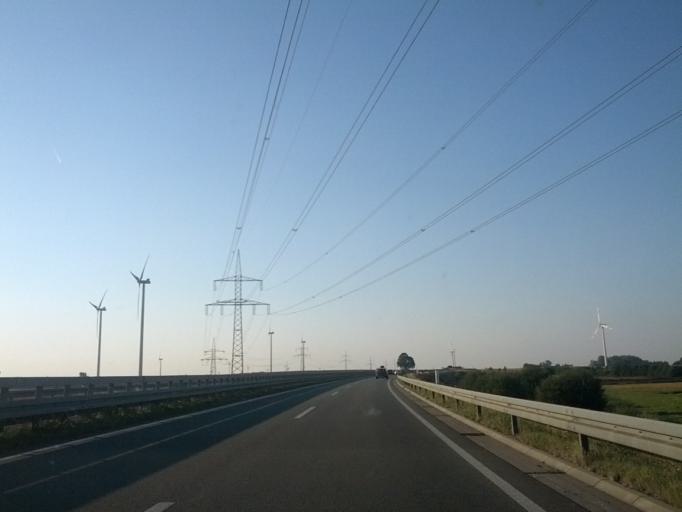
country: DE
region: Mecklenburg-Vorpommern
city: Brandshagen
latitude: 54.2016
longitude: 13.1566
